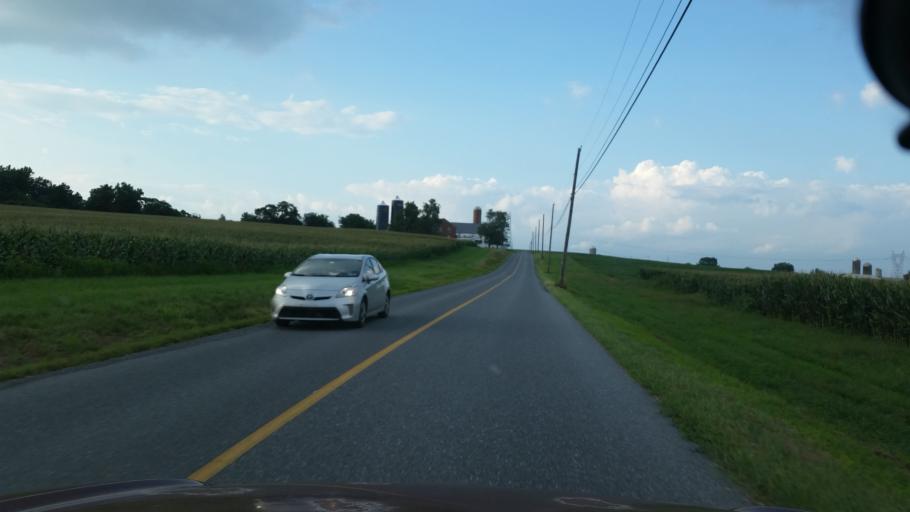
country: US
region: Pennsylvania
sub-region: Lancaster County
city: Mount Joy
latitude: 40.1290
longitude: -76.4677
